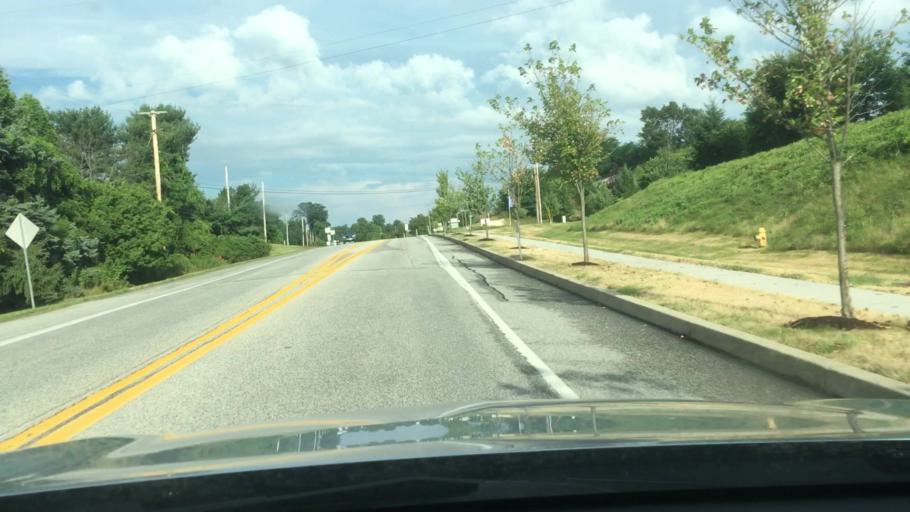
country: US
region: Pennsylvania
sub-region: York County
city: Dillsburg
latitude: 40.1061
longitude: -77.0252
